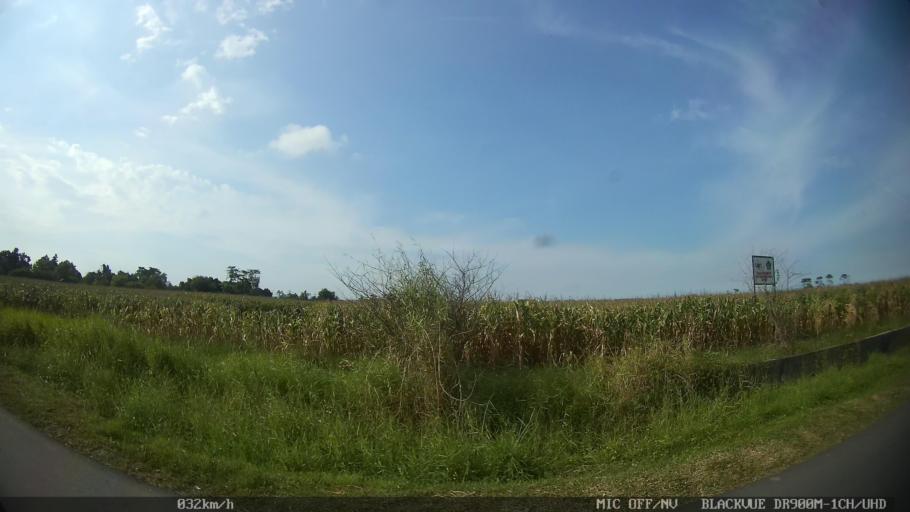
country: ID
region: North Sumatra
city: Percut
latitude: 3.5932
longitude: 98.7928
